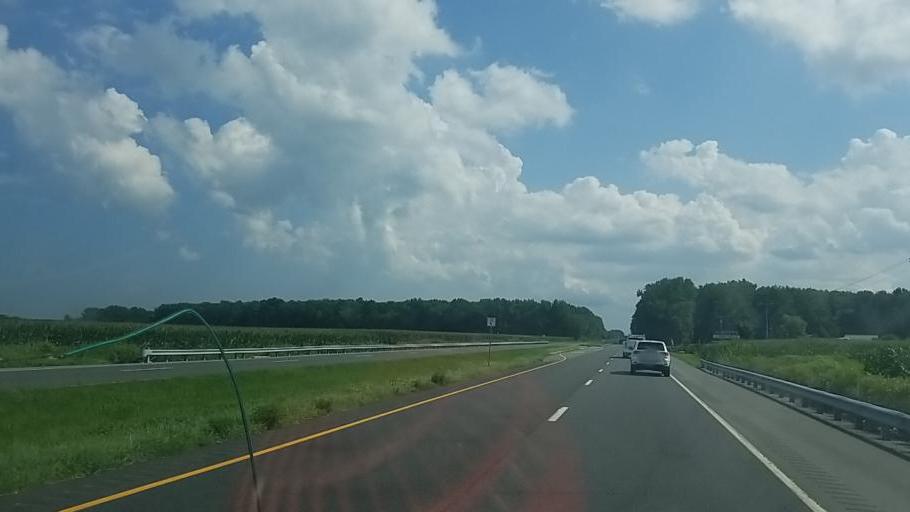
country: US
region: Delaware
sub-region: Sussex County
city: Selbyville
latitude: 38.4907
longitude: -75.2365
